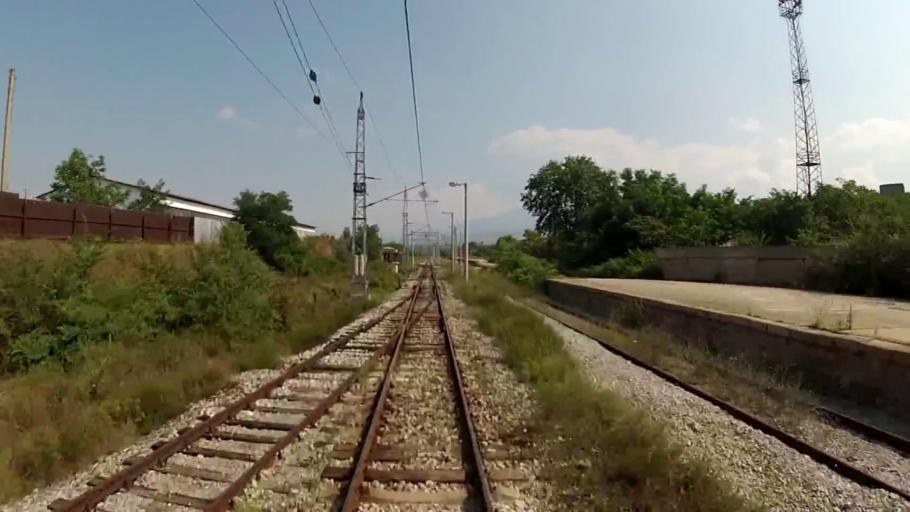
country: BG
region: Blagoevgrad
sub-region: Obshtina Sandanski
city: Sandanski
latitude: 41.5360
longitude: 23.2507
